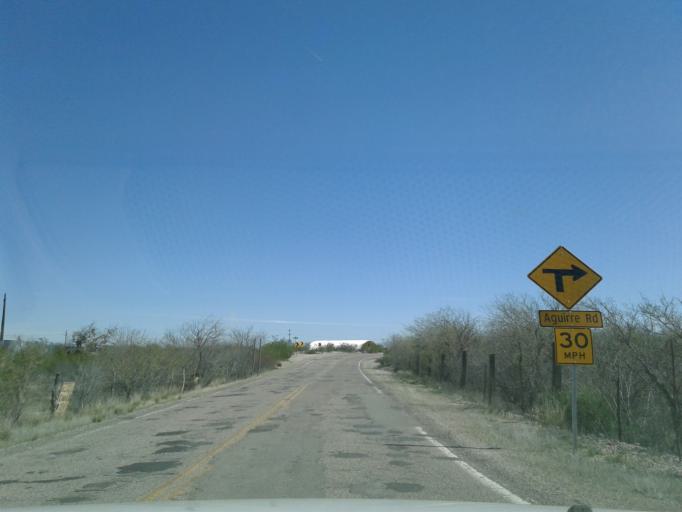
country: US
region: Arizona
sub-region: Pima County
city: Avra Valley
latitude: 32.4673
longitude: -111.3359
